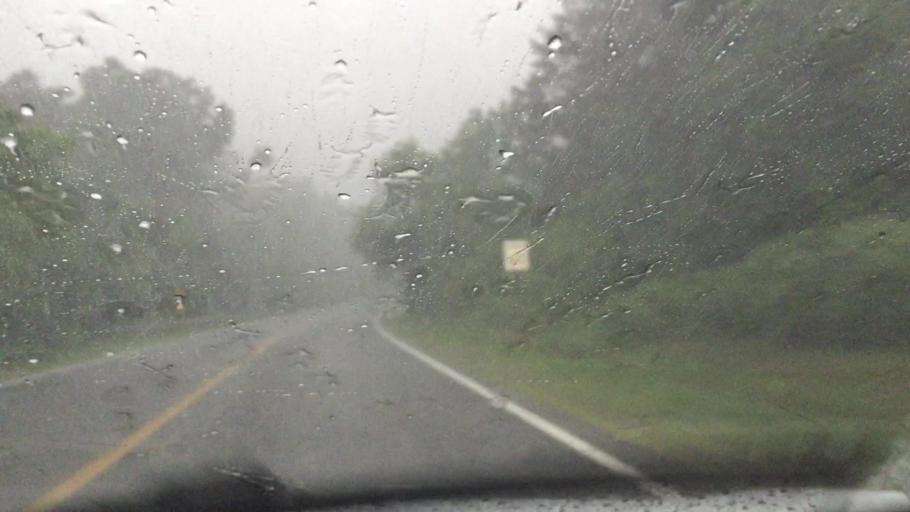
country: CA
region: Ontario
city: Markham
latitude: 43.8515
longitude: -79.2023
